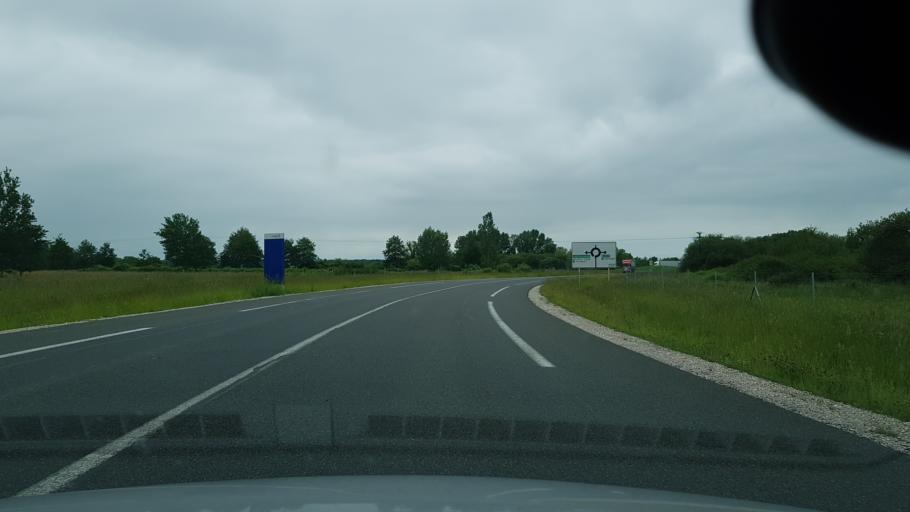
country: FR
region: Centre
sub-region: Departement du Loir-et-Cher
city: Chatillon-sur-Cher
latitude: 47.3224
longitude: 1.4997
